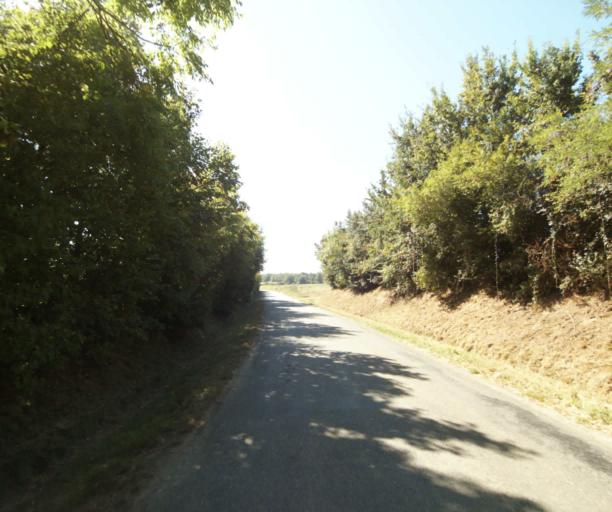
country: FR
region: Midi-Pyrenees
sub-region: Departement du Tarn-et-Garonne
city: Verdun-sur-Garonne
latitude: 43.8407
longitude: 1.2017
